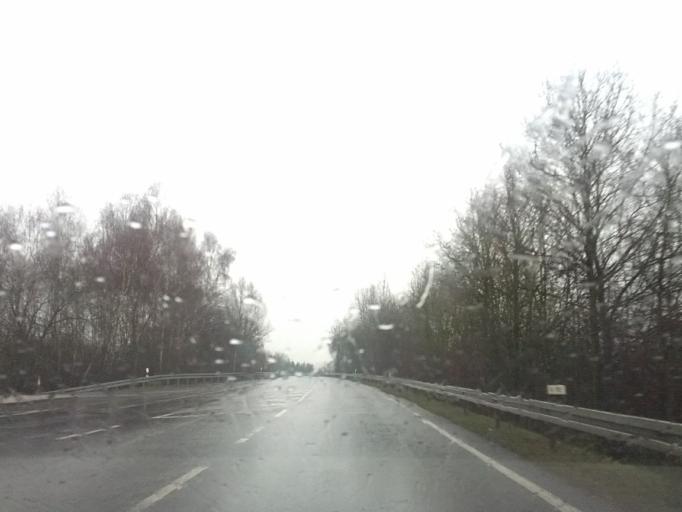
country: DE
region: Baden-Wuerttemberg
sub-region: Tuebingen Region
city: Biberach an der Riss
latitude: 48.0787
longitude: 9.8075
